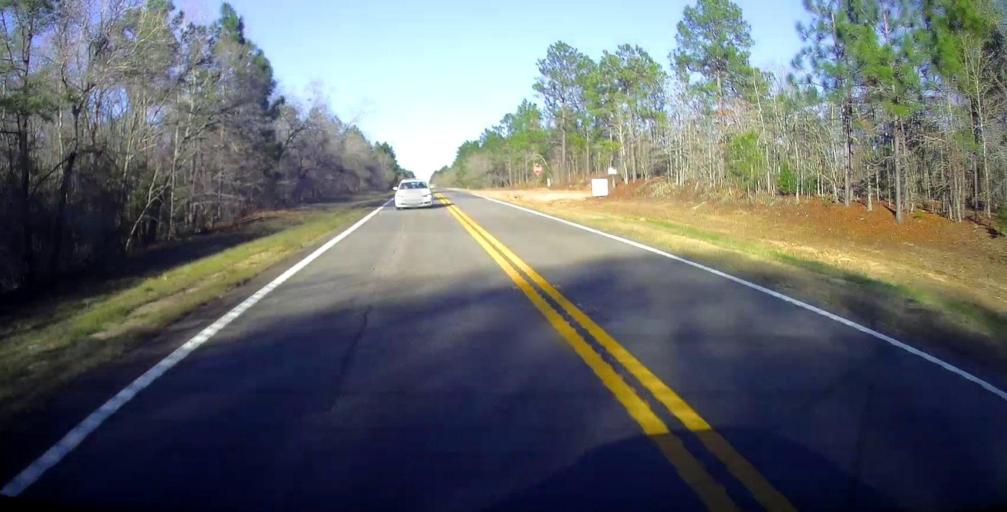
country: US
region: Georgia
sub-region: Taylor County
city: Butler
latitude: 32.5336
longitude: -84.2979
